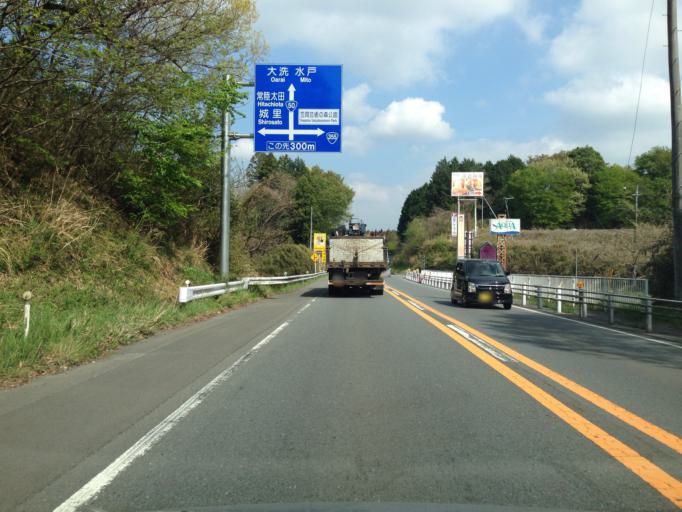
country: JP
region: Ibaraki
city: Kasama
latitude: 36.3912
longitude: 140.2806
